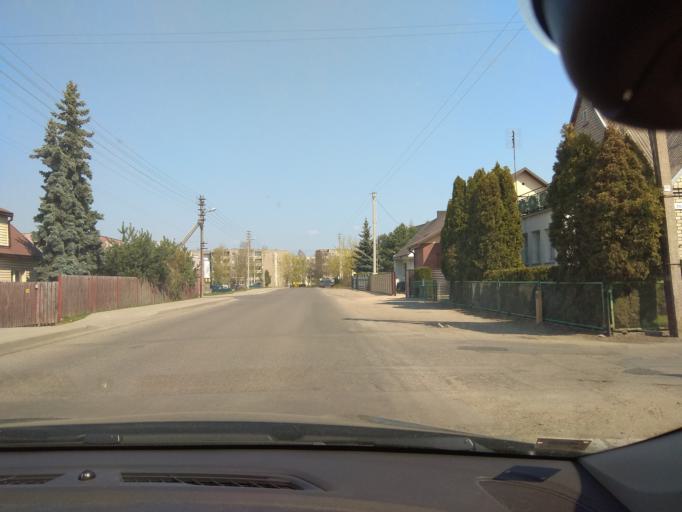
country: LT
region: Marijampoles apskritis
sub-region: Marijampole Municipality
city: Marijampole
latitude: 54.5658
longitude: 23.3504
